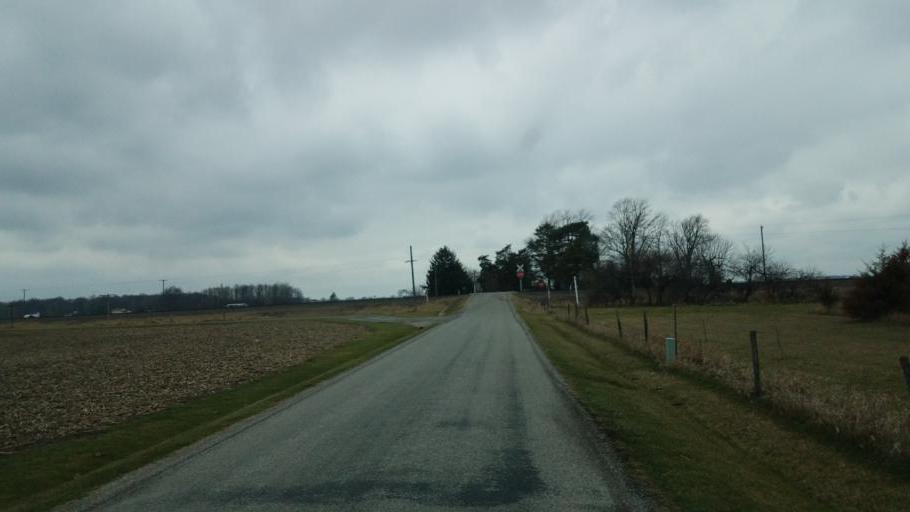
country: US
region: Ohio
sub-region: Delaware County
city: Ashley
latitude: 40.3765
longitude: -82.9752
